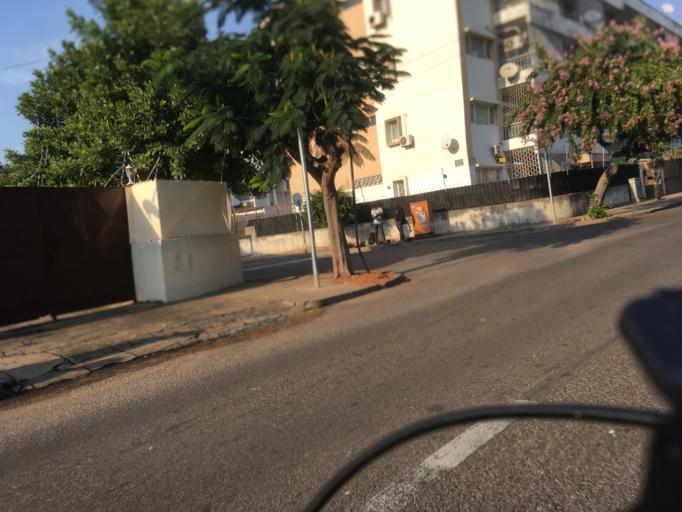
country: MZ
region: Maputo City
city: Maputo
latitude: -25.9528
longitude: 32.5921
